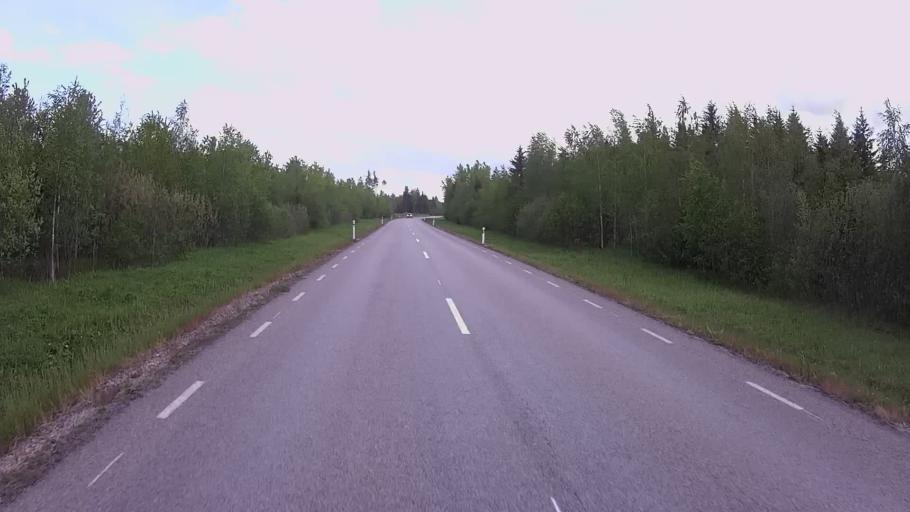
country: EE
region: Jogevamaa
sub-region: Mustvee linn
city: Mustvee
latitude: 59.0818
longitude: 26.9916
